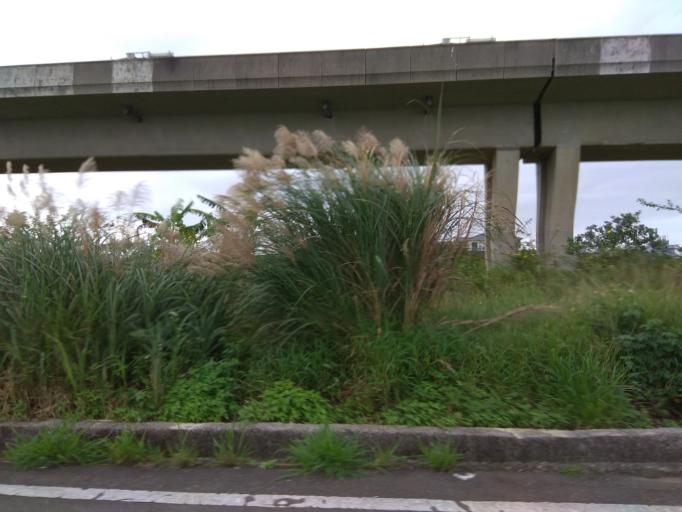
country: TW
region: Taiwan
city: Taoyuan City
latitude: 25.0451
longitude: 121.2150
